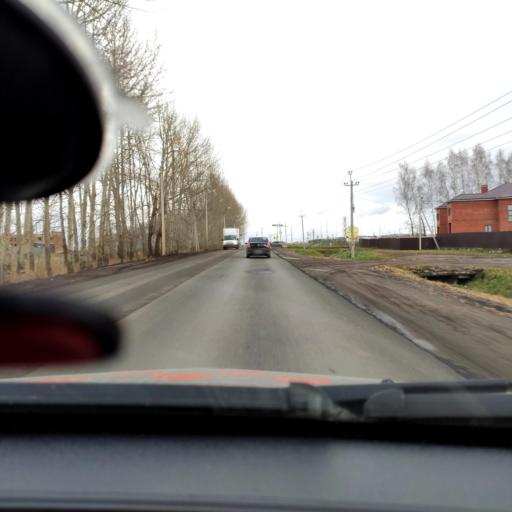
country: RU
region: Bashkortostan
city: Kabakovo
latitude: 54.6184
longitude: 56.1220
